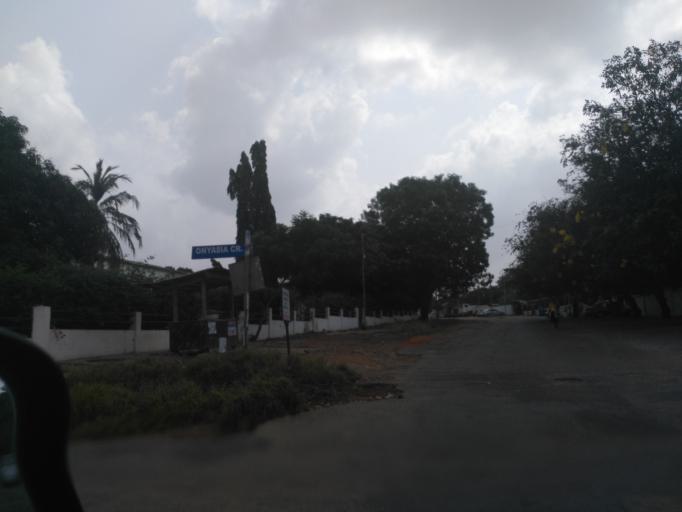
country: GH
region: Greater Accra
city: Accra
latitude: 5.5999
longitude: -0.1942
